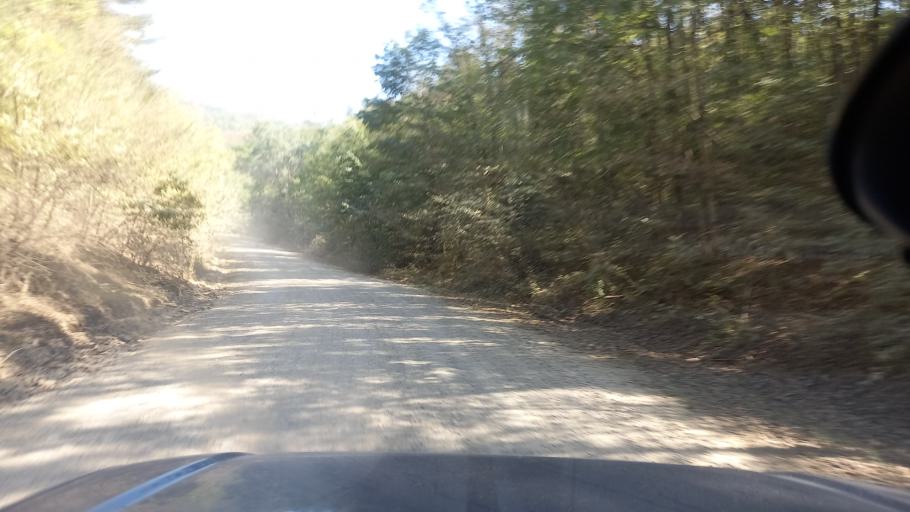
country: RU
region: Krasnodarskiy
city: Azovskaya
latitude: 44.6766
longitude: 38.6339
